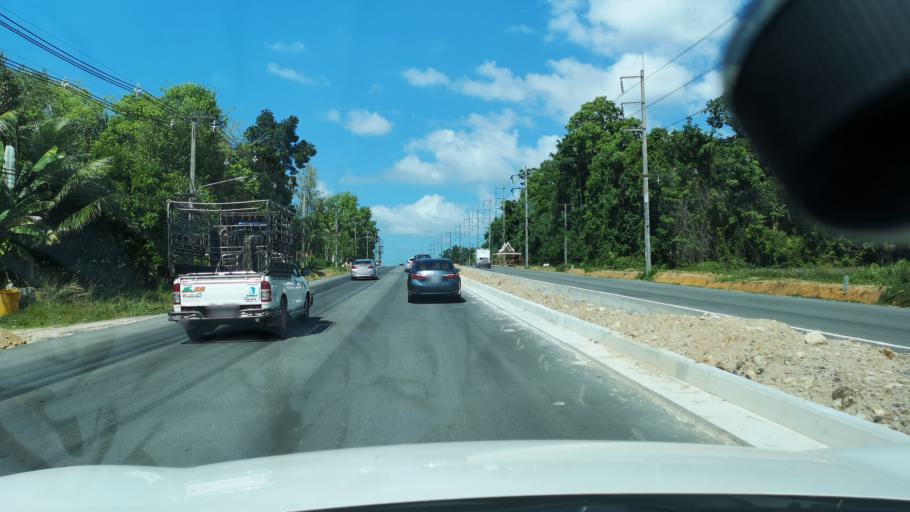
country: TH
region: Phangnga
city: Thai Mueang
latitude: 8.4278
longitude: 98.2583
